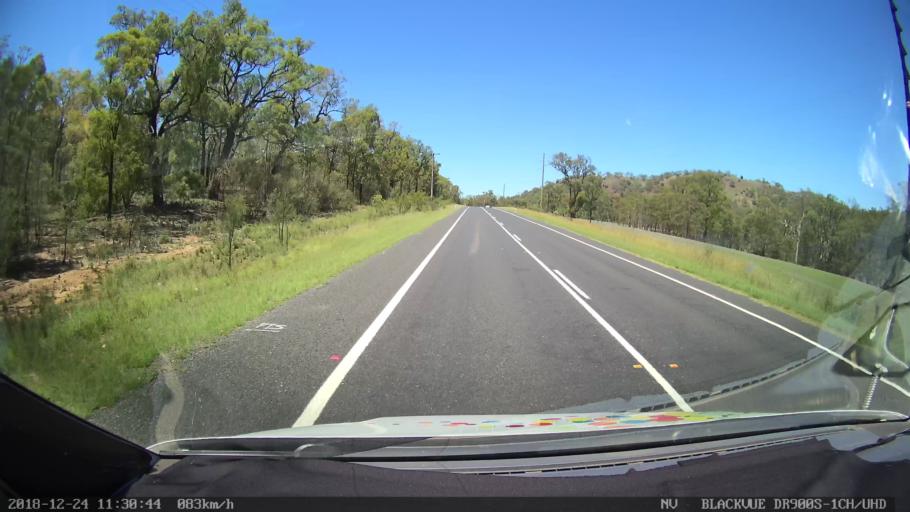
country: AU
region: New South Wales
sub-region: Upper Hunter Shire
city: Merriwa
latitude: -32.2078
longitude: 150.4641
